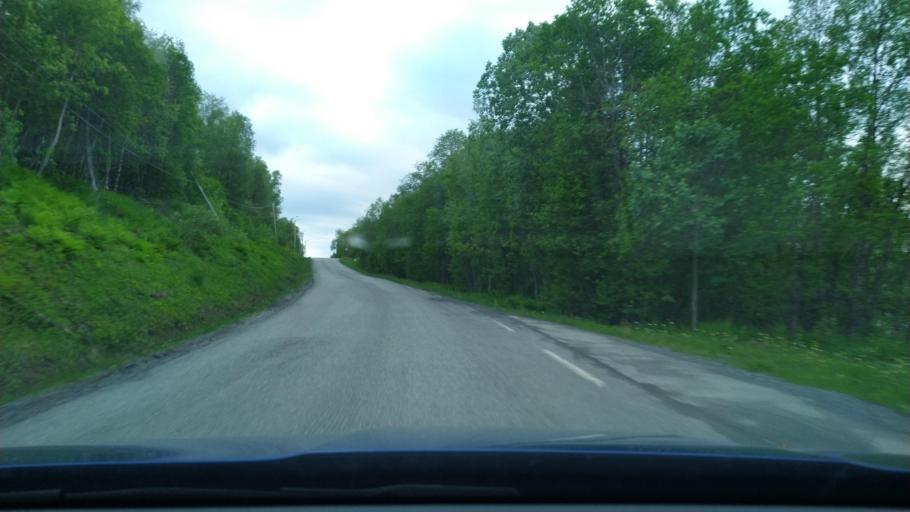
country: NO
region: Troms
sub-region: Tranoy
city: Vangsvika
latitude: 69.1297
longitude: 17.8656
